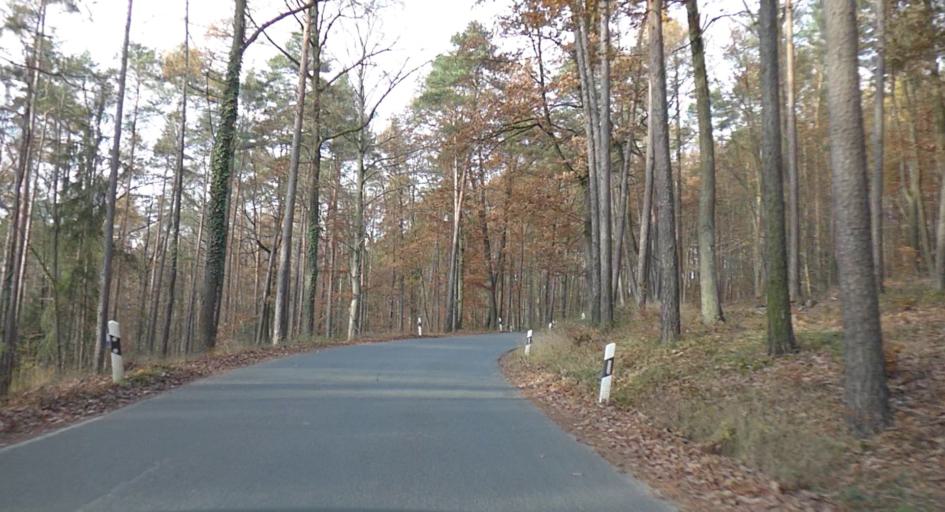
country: DE
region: Bavaria
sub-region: Regierungsbezirk Mittelfranken
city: Bubenreuth
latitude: 49.6141
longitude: 11.0238
